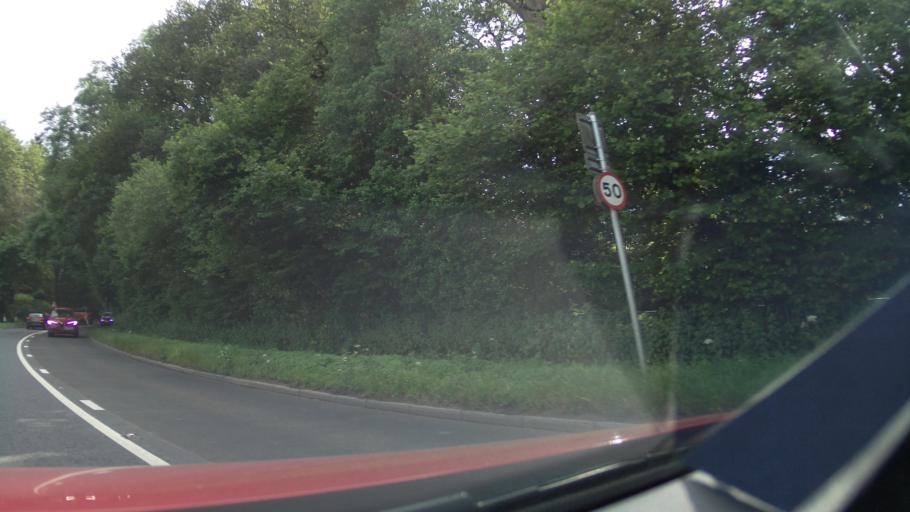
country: GB
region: England
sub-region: Worcestershire
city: Kidderminster
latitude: 52.4253
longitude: -2.2128
